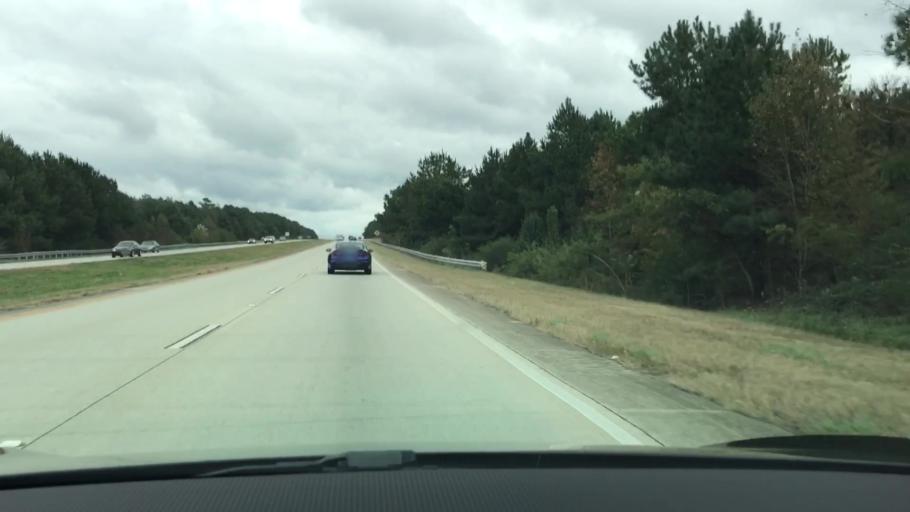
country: US
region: Georgia
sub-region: Oconee County
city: Bogart
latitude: 33.9241
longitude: -83.5103
